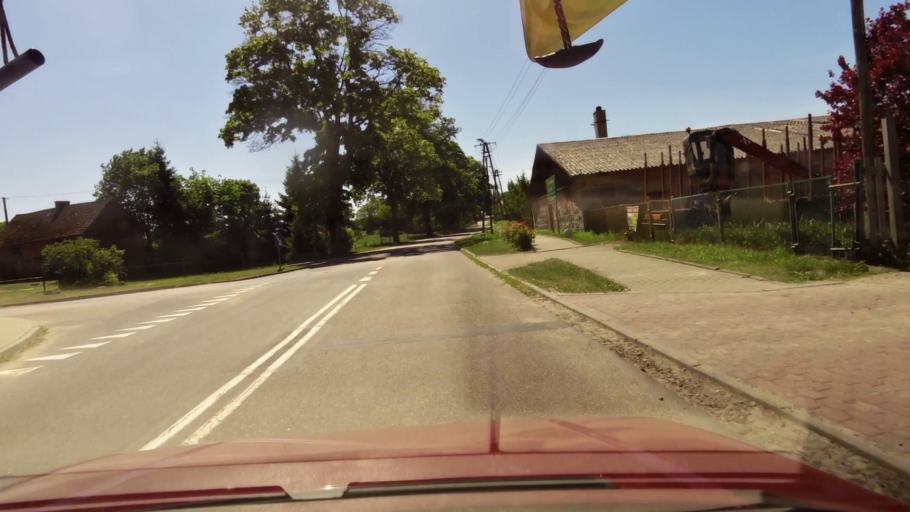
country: PL
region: West Pomeranian Voivodeship
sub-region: Powiat koszalinski
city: Bobolice
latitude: 53.9913
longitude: 16.6872
